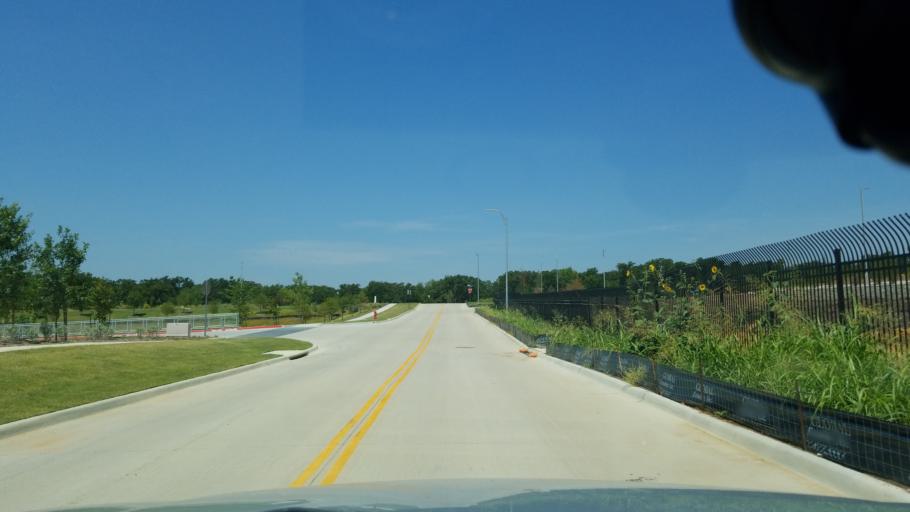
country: US
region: Texas
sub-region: Tarrant County
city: Euless
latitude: 32.8420
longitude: -97.0293
